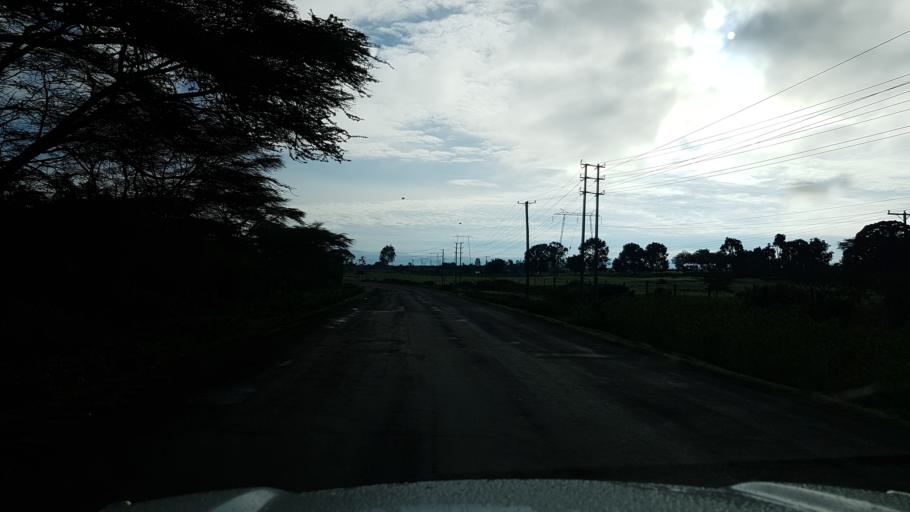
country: KE
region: Nakuru
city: Naivasha
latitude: -0.8236
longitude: 36.3828
